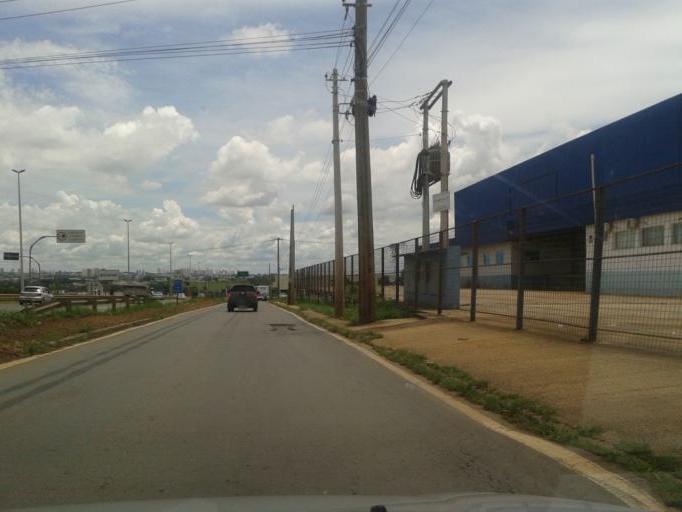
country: BR
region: Goias
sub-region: Aparecida De Goiania
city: Aparecida de Goiania
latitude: -16.7895
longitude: -49.2376
